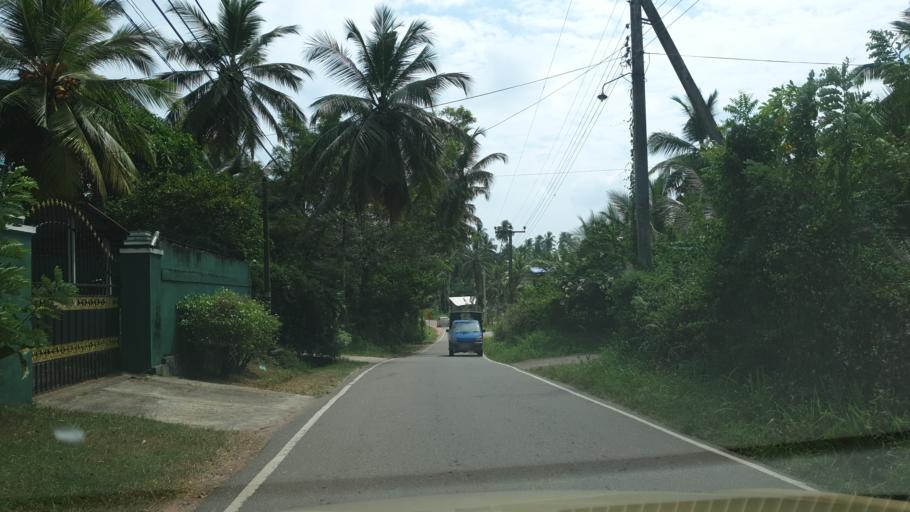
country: LK
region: North Western
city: Kuliyapitiya
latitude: 7.3487
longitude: 79.9792
